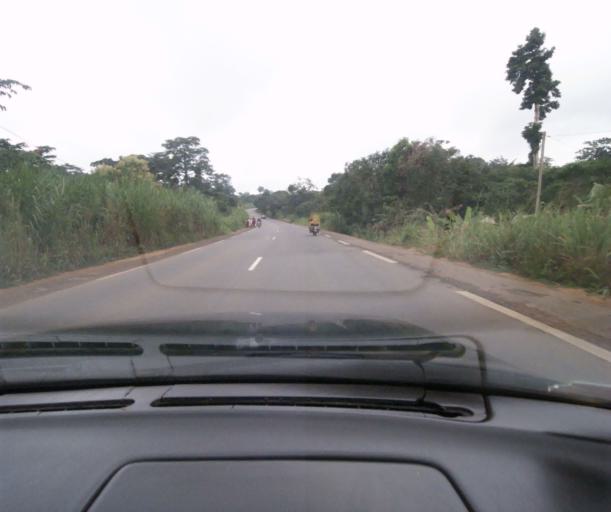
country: CM
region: Centre
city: Obala
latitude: 4.1660
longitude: 11.4923
